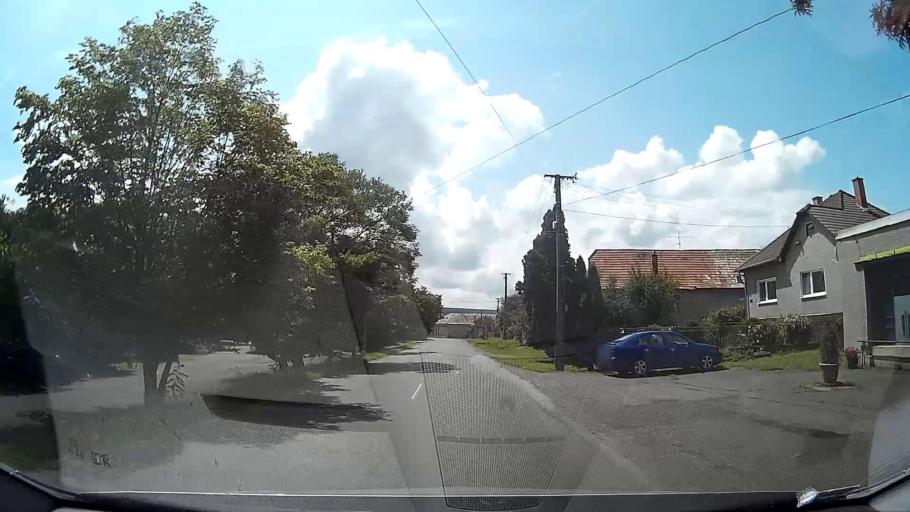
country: SK
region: Banskobystricky
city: Fil'akovo
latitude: 48.3008
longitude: 19.7915
